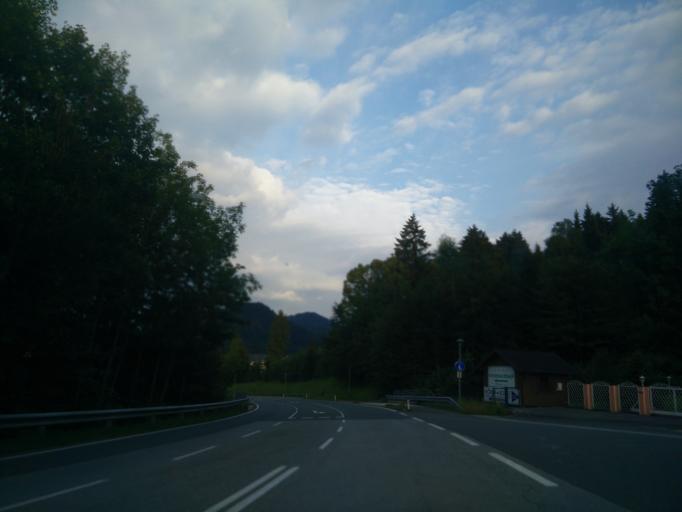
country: AT
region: Salzburg
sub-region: Politischer Bezirk Salzburg-Umgebung
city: Fuschl am See
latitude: 47.7932
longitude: 13.2836
